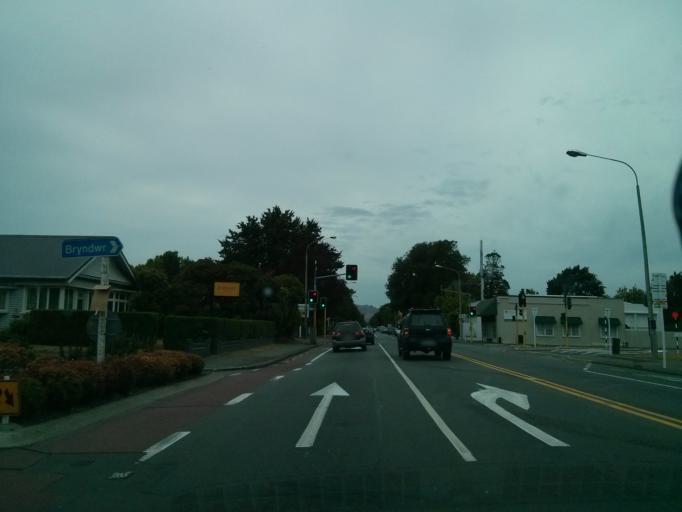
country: NZ
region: Canterbury
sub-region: Christchurch City
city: Christchurch
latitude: -43.4997
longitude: 172.6104
